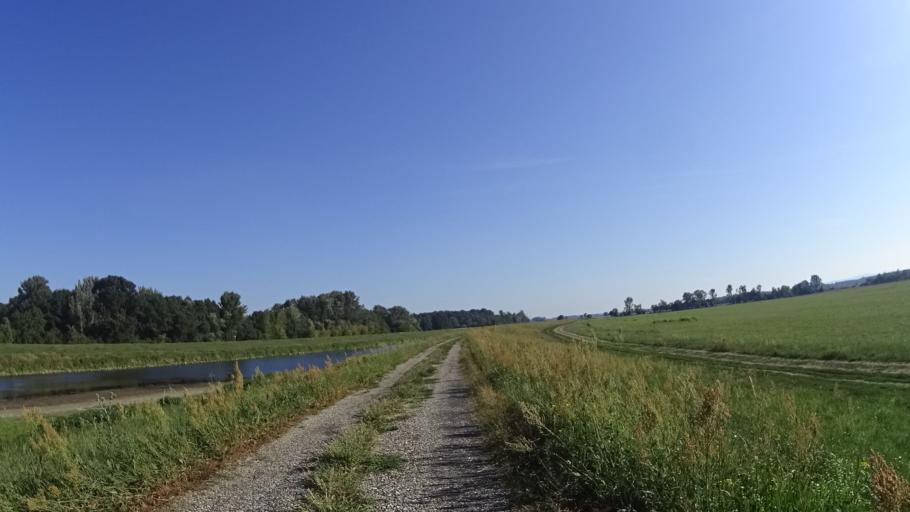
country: CZ
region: South Moravian
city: Tvrdonice
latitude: 48.7287
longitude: 17.0152
